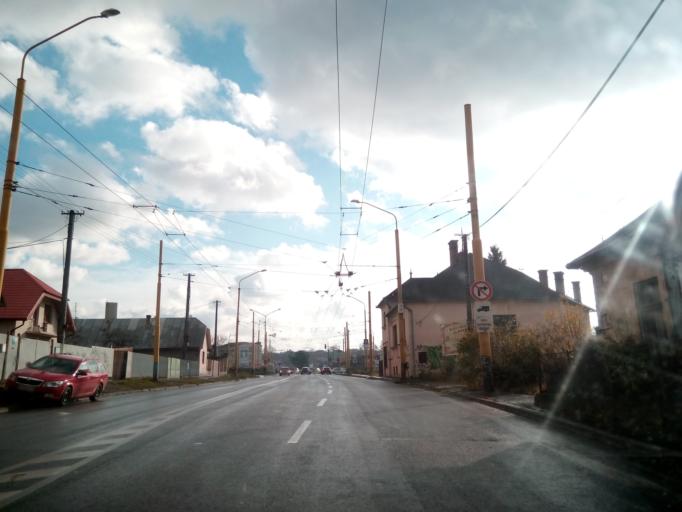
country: SK
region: Presovsky
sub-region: Okres Presov
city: Presov
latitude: 48.9784
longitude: 21.2622
